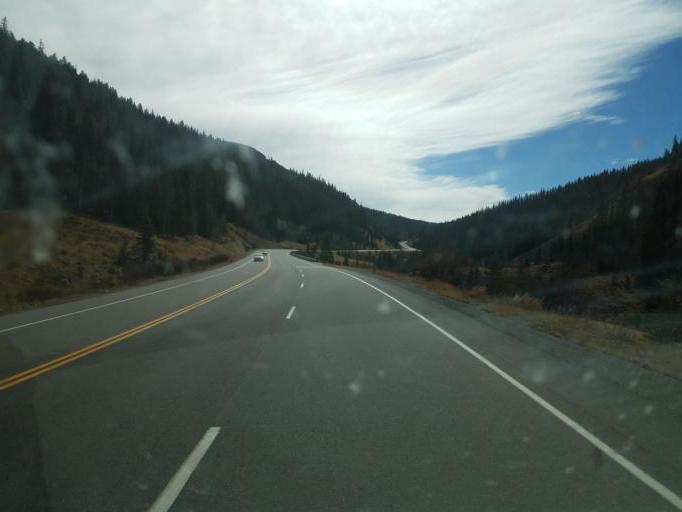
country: US
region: Colorado
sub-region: Mineral County
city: Creede
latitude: 37.5379
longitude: -106.7725
